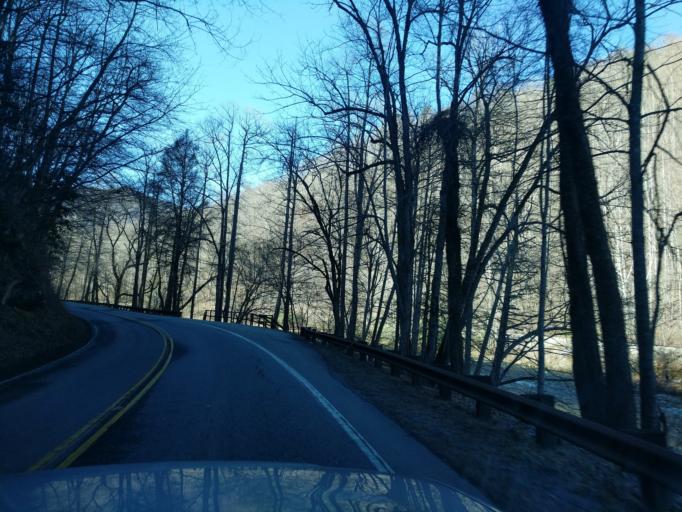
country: US
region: North Carolina
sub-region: Swain County
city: Bryson City
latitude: 35.3314
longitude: -83.6018
